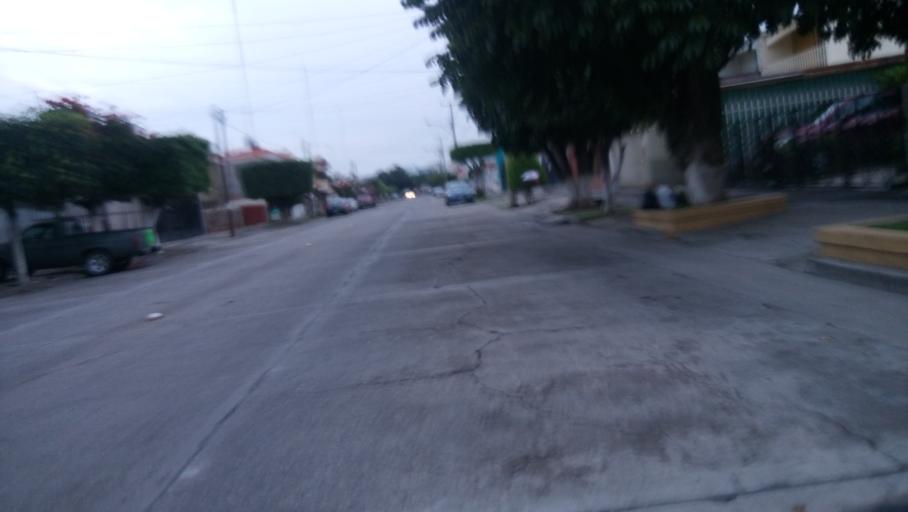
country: MX
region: Guanajuato
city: Leon
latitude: 21.1472
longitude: -101.6686
